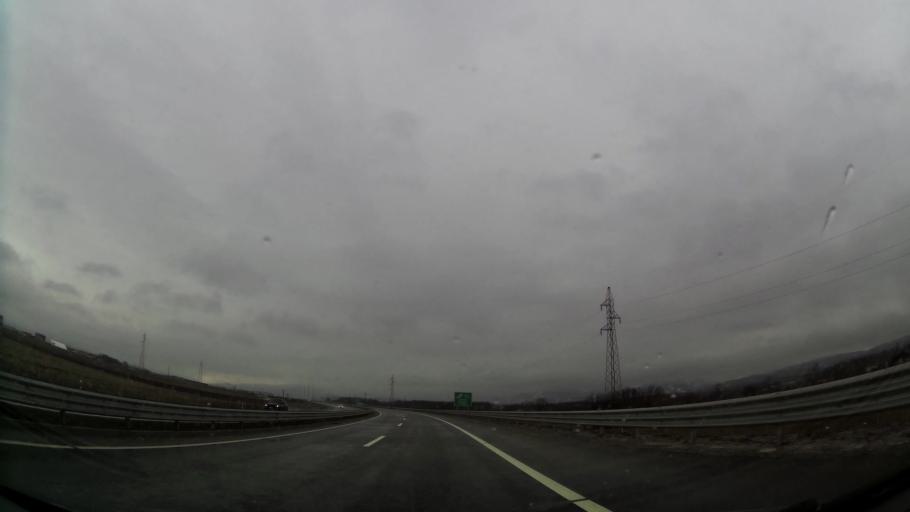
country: XK
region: Ferizaj
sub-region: Komuna e Kacanikut
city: Kacanik
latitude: 42.2978
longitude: 21.2040
